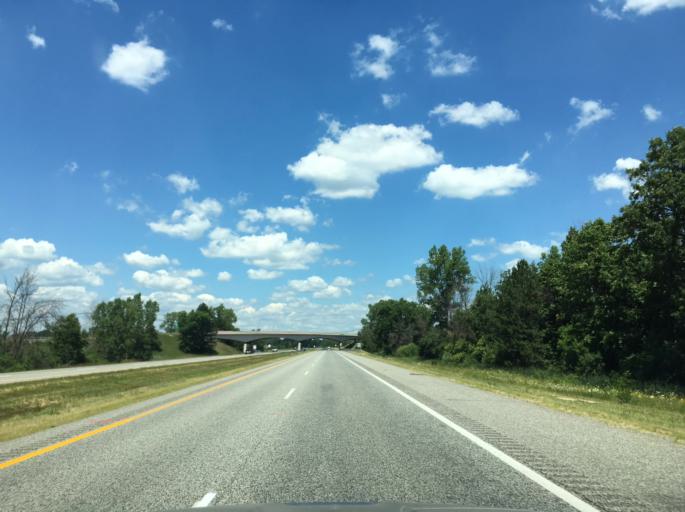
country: US
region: Michigan
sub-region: Midland County
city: Midland
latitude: 43.6382
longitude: -84.1855
